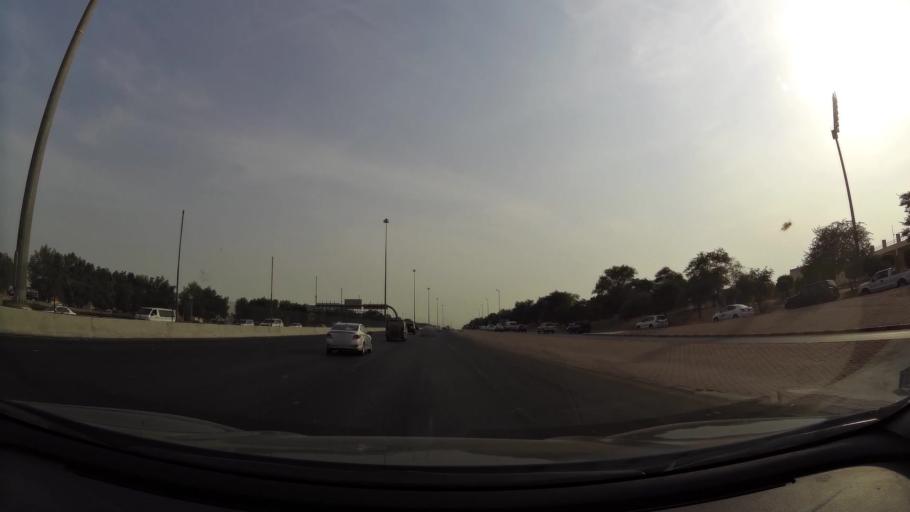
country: KW
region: Al Farwaniyah
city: Janub as Surrah
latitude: 29.2825
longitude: 47.9856
